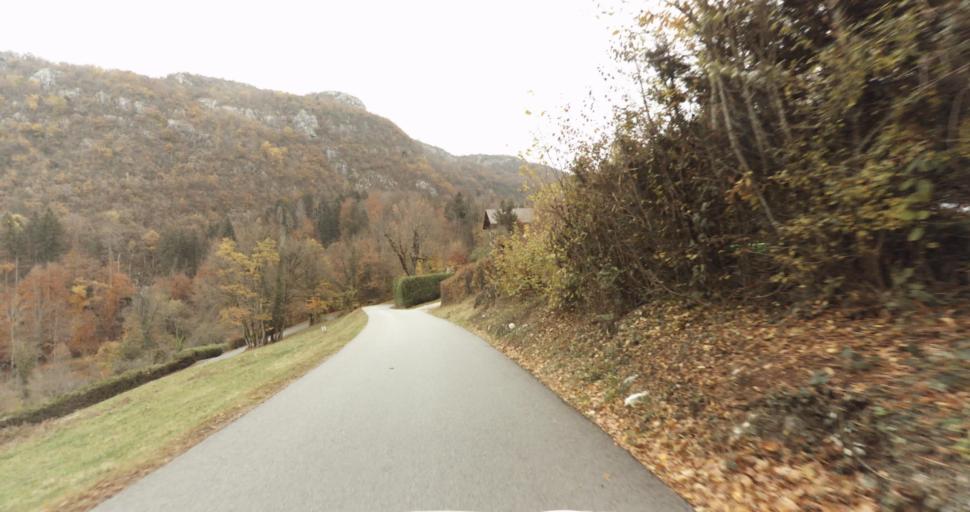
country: FR
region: Rhone-Alpes
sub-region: Departement de la Haute-Savoie
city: Talloires
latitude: 45.8185
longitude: 6.1957
